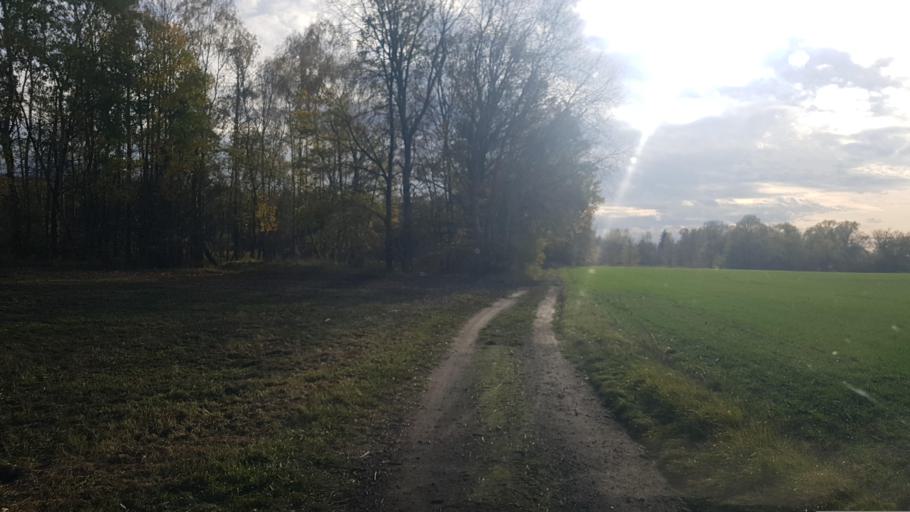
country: DE
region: Brandenburg
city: Wiesenburg
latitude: 52.0775
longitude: 12.4640
